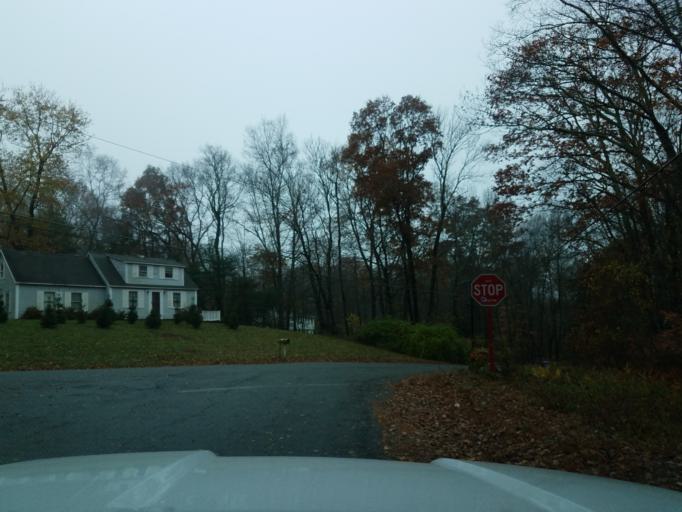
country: US
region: Connecticut
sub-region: Windham County
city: Windham
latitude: 41.7829
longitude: -72.1078
